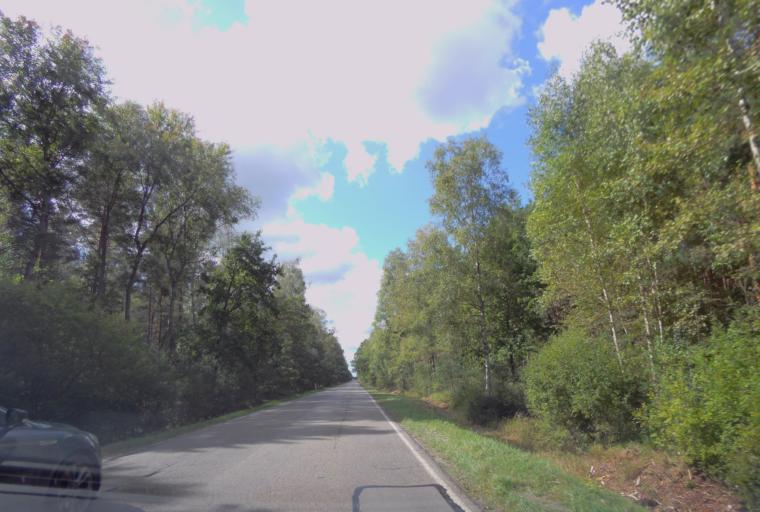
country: PL
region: Subcarpathian Voivodeship
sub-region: Powiat stalowowolski
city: Bojanow
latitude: 50.4234
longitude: 21.9027
